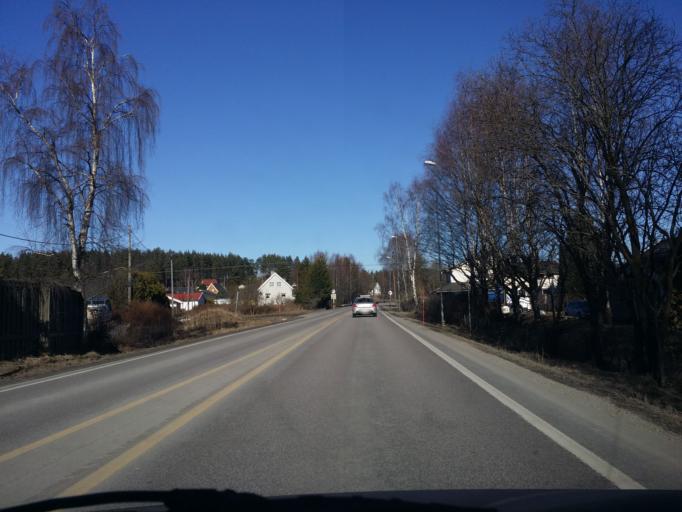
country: NO
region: Buskerud
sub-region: Ringerike
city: Honefoss
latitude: 60.2054
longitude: 10.2585
